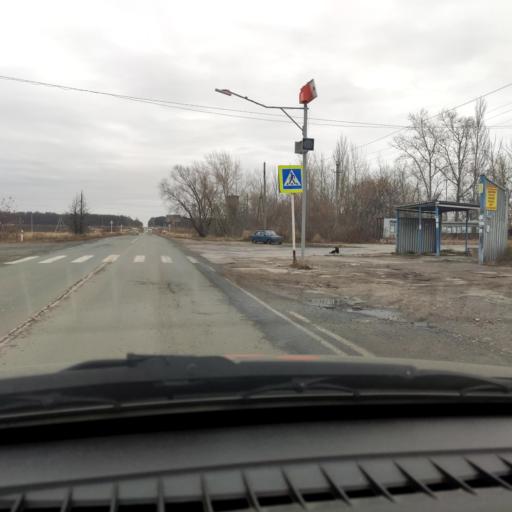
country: RU
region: Samara
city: Zhigulevsk
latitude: 53.3404
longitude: 49.4705
